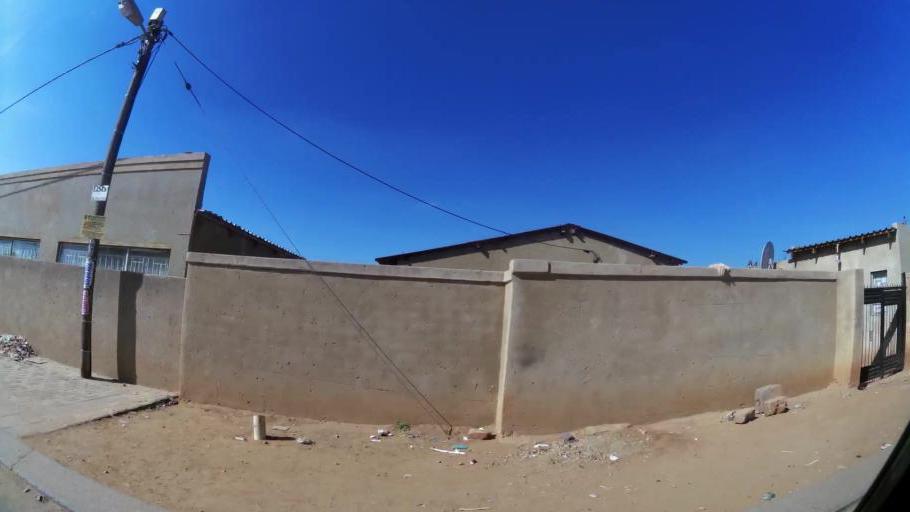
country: ZA
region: Gauteng
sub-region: West Rand District Municipality
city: Muldersdriseloop
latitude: -26.0277
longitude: 27.9282
